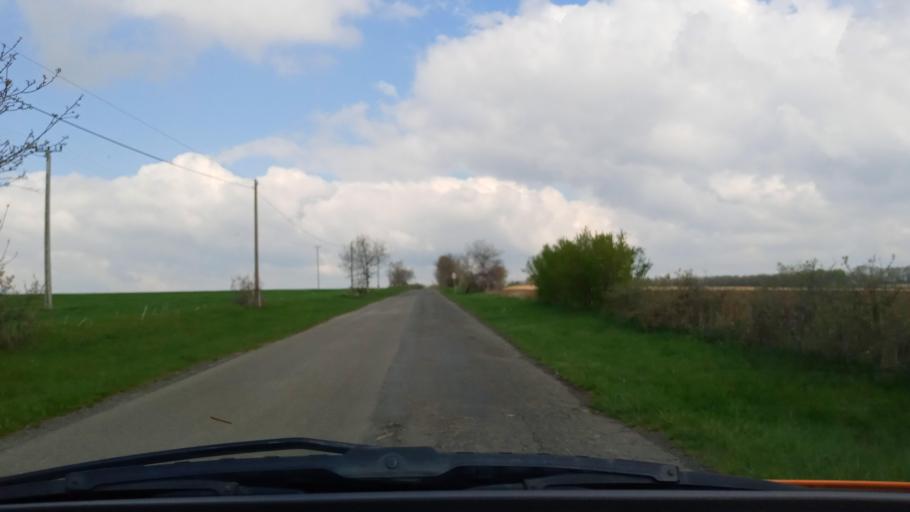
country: HU
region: Baranya
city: Pecsvarad
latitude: 46.1003
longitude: 18.4975
